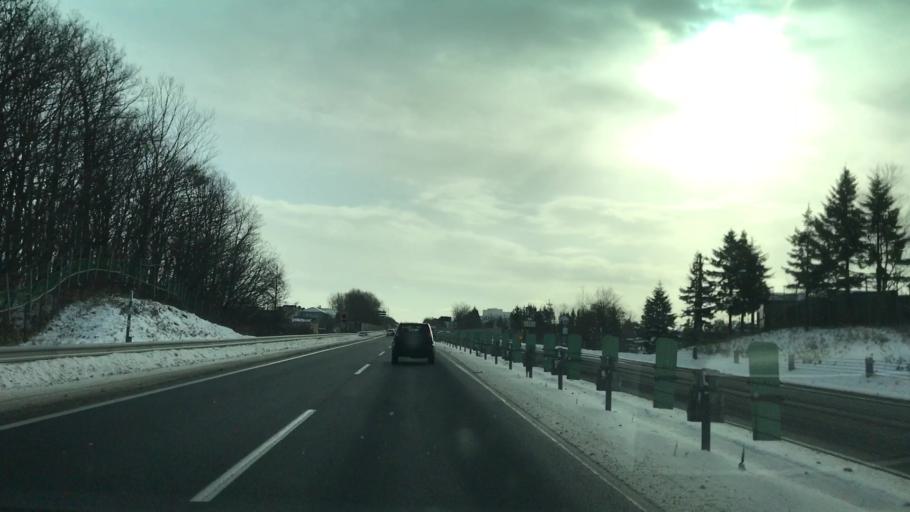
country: JP
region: Hokkaido
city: Kitahiroshima
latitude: 42.9742
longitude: 141.4819
